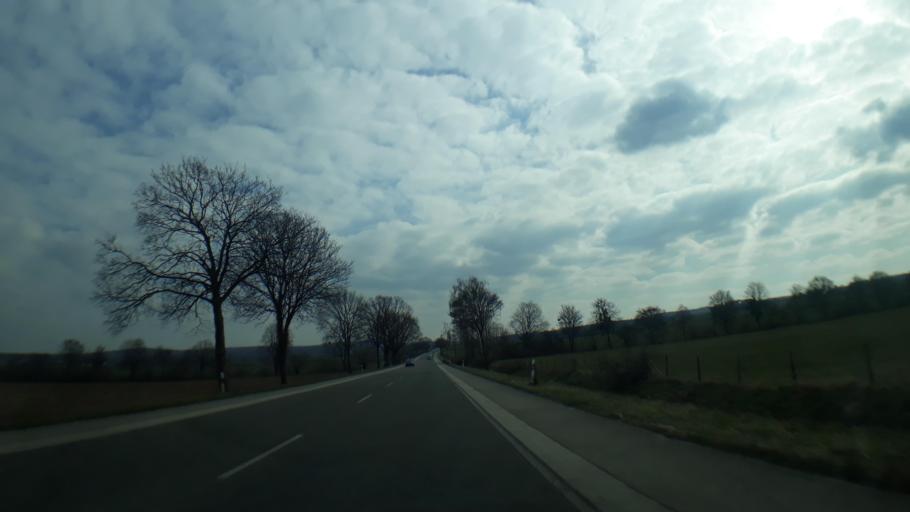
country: DE
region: North Rhine-Westphalia
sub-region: Regierungsbezirk Koln
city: Euskirchen
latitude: 50.6141
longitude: 6.8446
